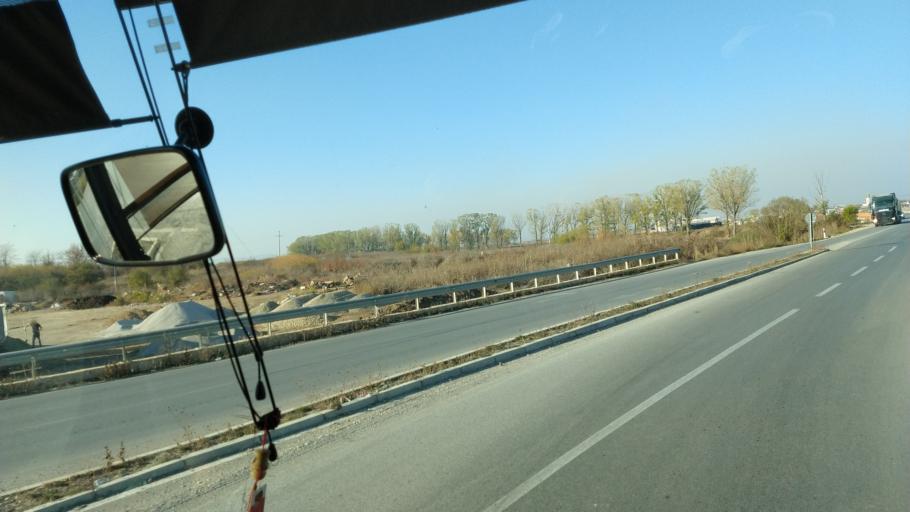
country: XK
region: Pristina
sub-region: Lipjan
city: Lipljan
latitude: 42.5115
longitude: 21.1128
